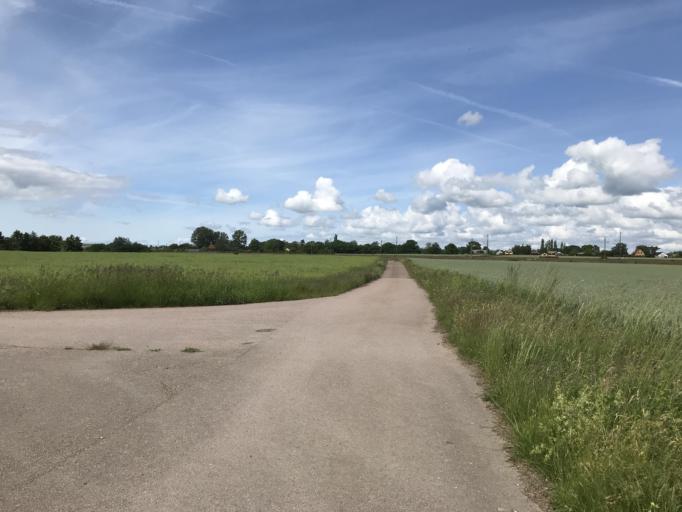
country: SE
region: Skane
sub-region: Landskrona
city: Landskrona
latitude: 55.8987
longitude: 12.8483
